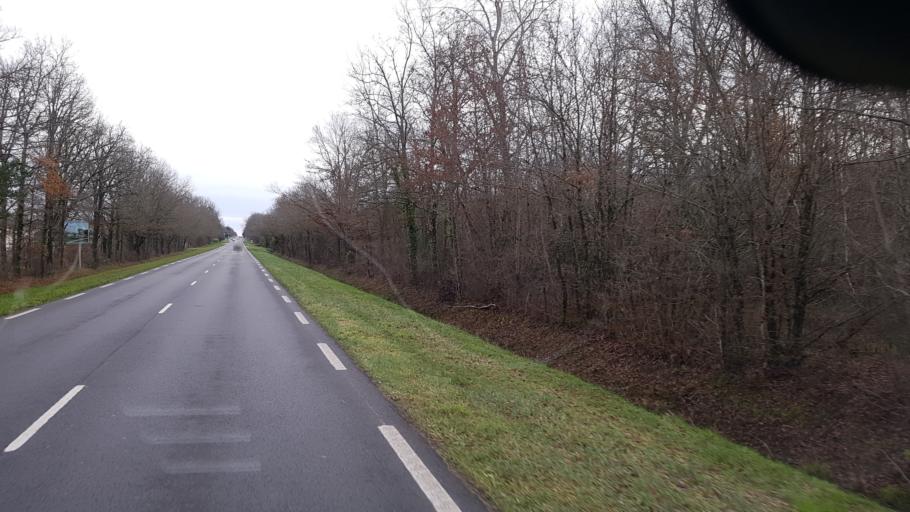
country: FR
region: Centre
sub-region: Departement du Loiret
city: Menestreau-en-Villette
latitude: 47.6581
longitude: 1.9830
